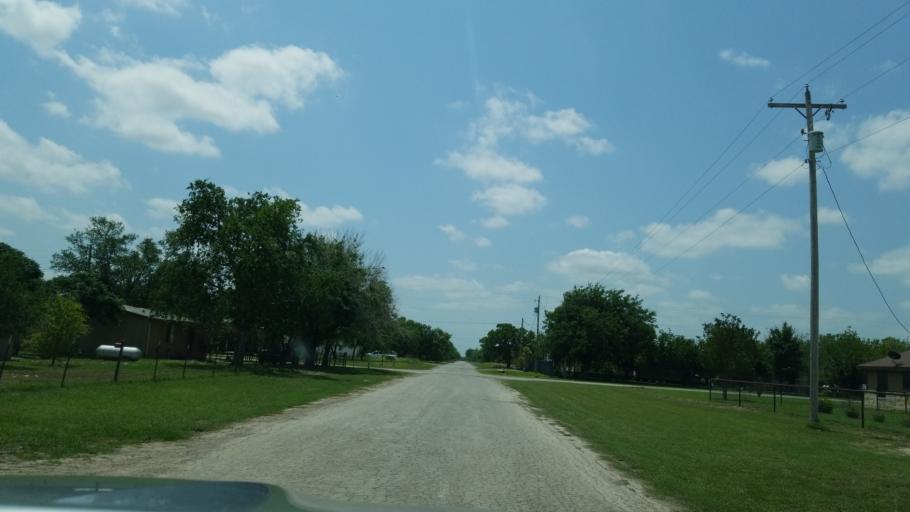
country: US
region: Texas
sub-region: Zavala County
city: La Pryor
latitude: 28.9423
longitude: -99.8414
